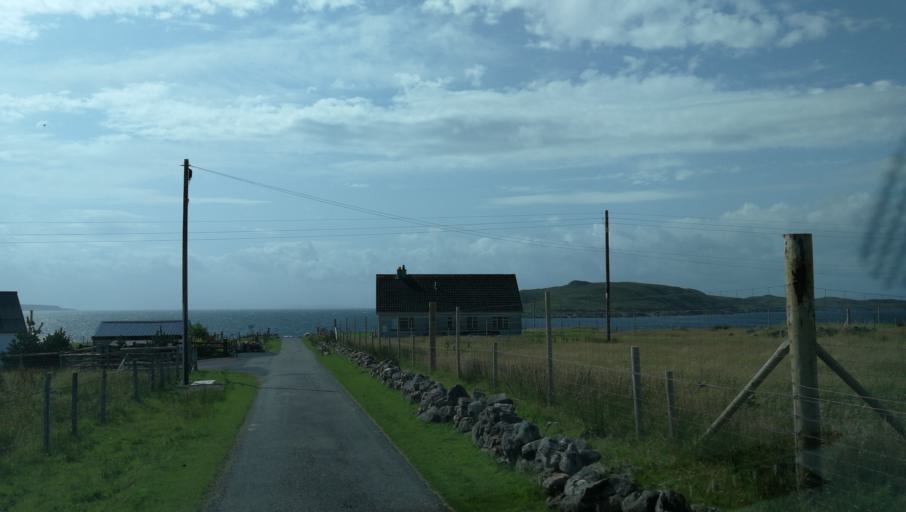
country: GB
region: Scotland
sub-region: Highland
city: Portree
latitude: 57.7433
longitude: -5.7767
